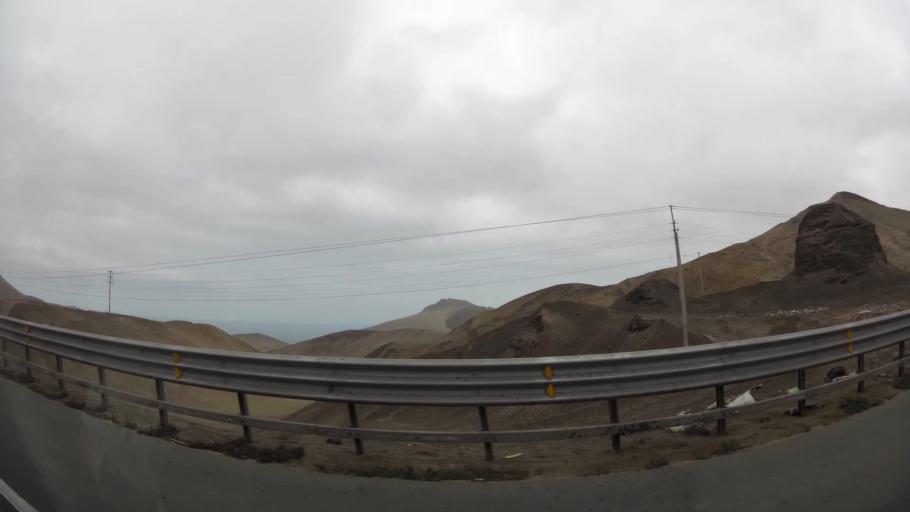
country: PE
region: Lima
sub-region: Lima
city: San Bartolo
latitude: -12.4320
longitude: -76.7539
